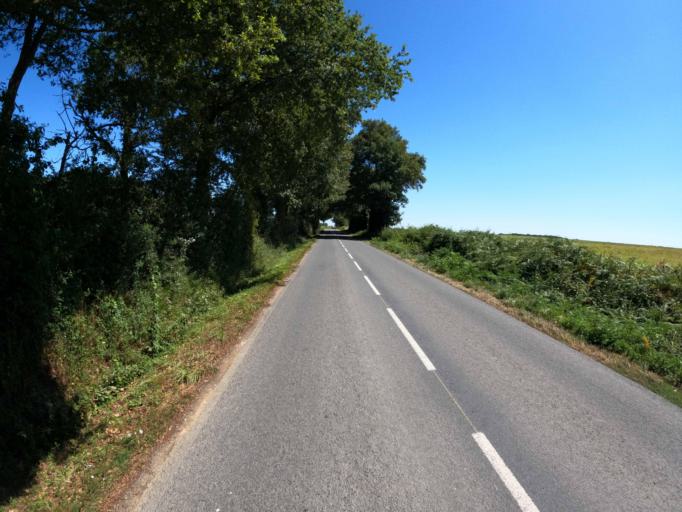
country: FR
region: Pays de la Loire
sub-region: Departement de la Loire-Atlantique
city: La Limouziniere
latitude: 46.9706
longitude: -1.5695
